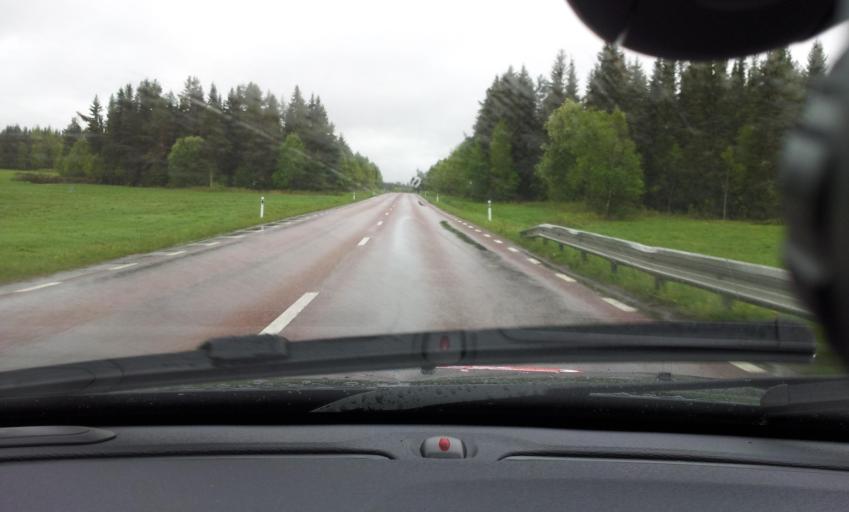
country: SE
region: Jaemtland
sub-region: Bergs Kommun
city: Hoverberg
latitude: 62.9081
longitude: 14.5227
